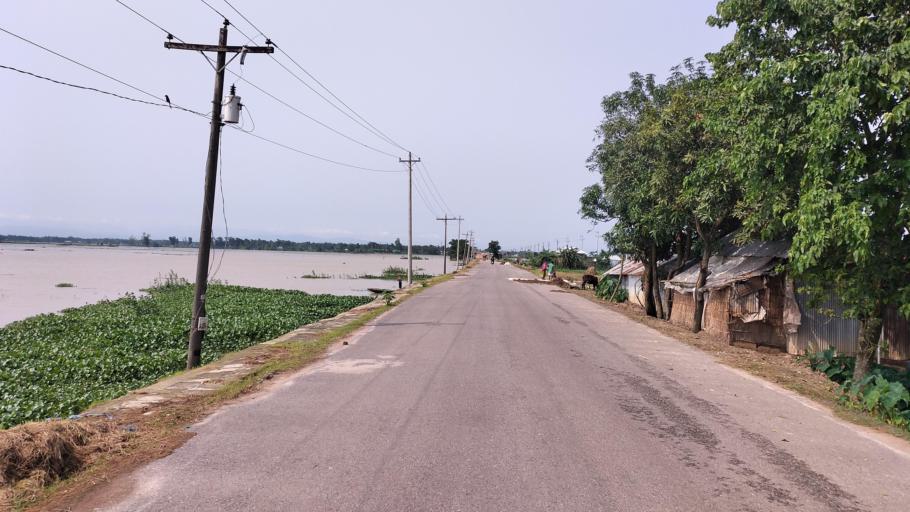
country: BD
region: Dhaka
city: Netrakona
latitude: 25.0172
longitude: 90.8562
